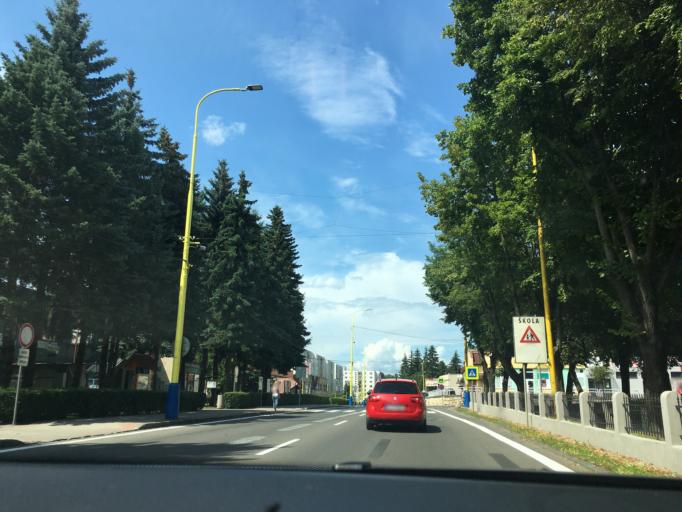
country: SK
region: Presovsky
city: Stropkov
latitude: 49.2023
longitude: 21.6517
